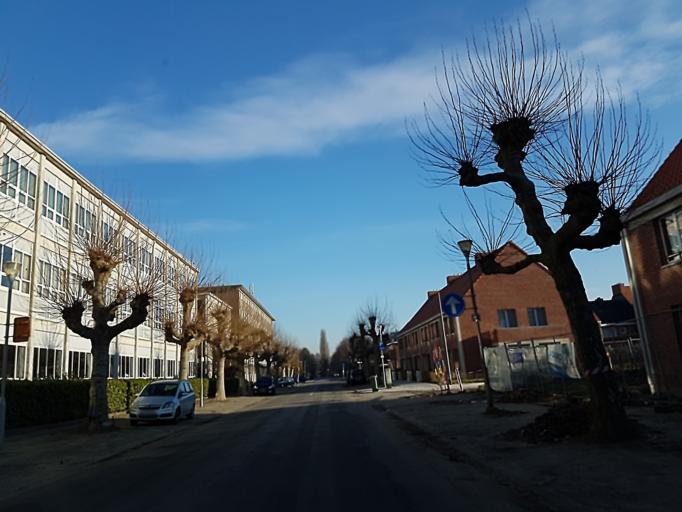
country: BE
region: Flanders
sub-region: Provincie Antwerpen
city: Hoboken
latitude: 51.1731
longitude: 4.3676
